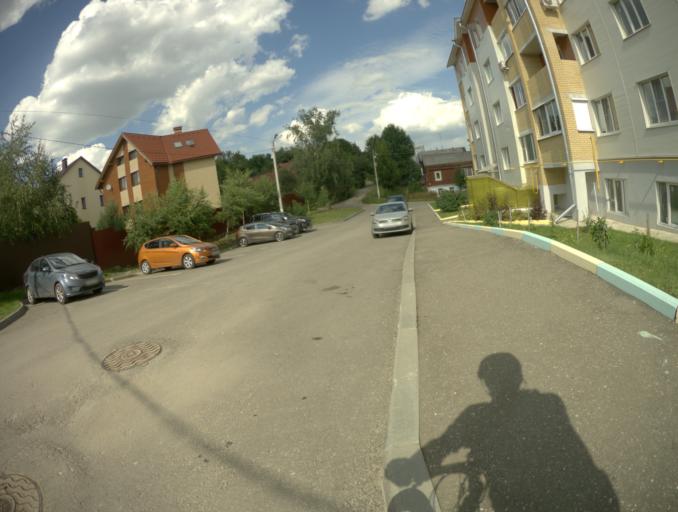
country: RU
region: Vladimir
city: Vladimir
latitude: 56.1130
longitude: 40.3694
